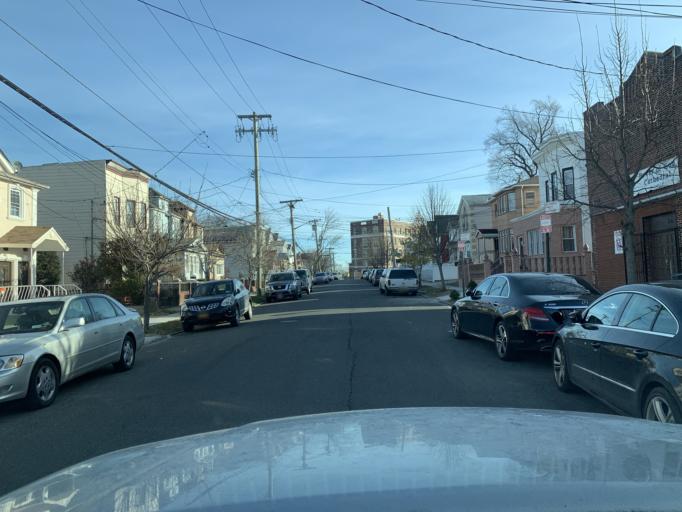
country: US
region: New York
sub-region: Queens County
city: Jamaica
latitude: 40.7004
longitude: -73.7847
